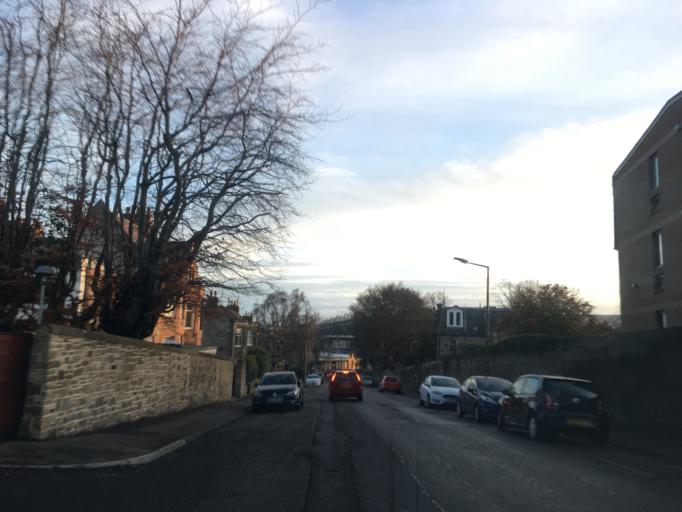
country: GB
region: Scotland
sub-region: Edinburgh
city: Colinton
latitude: 55.9466
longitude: -3.2455
